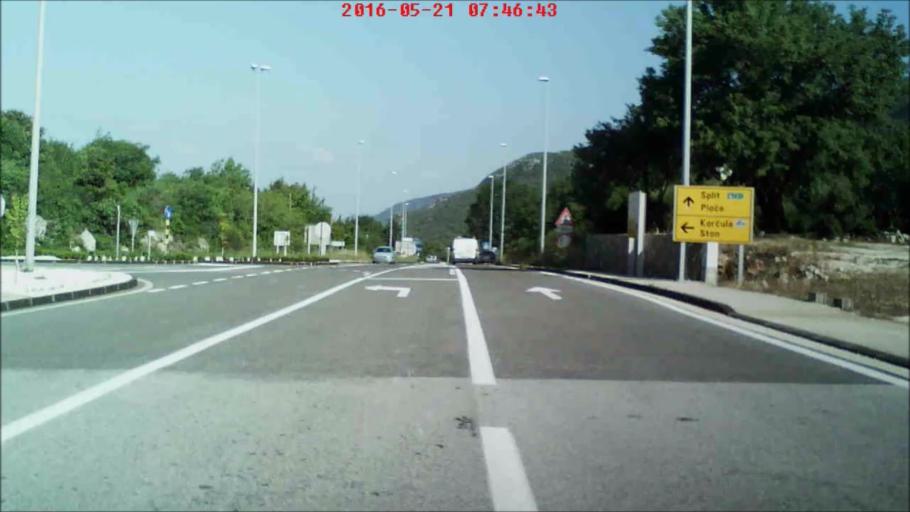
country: HR
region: Dubrovacko-Neretvanska
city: Ston
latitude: 42.8317
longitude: 17.7506
